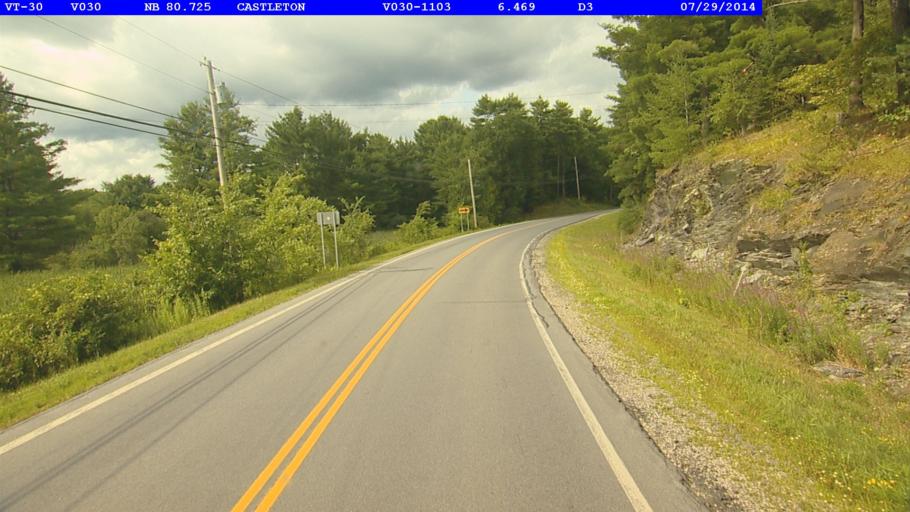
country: US
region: Vermont
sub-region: Rutland County
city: Castleton
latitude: 43.6779
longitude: -73.1913
